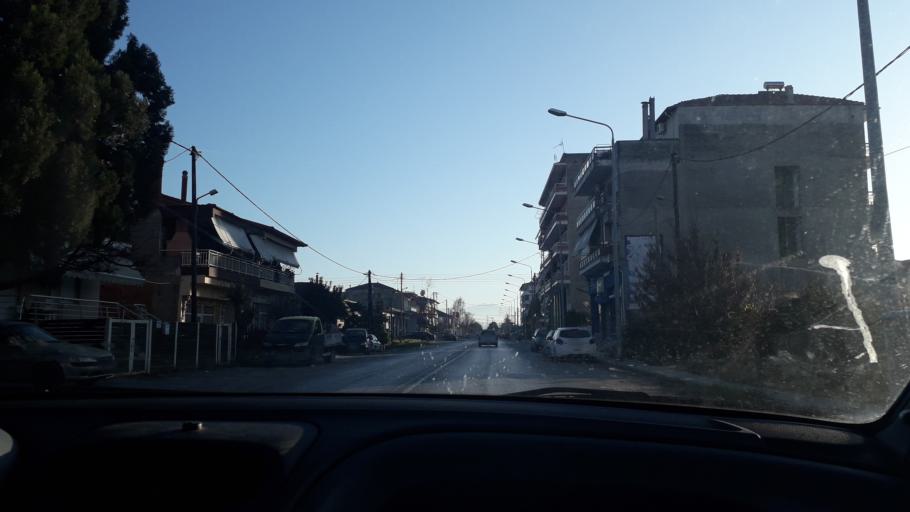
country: GR
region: Central Macedonia
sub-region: Nomos Imathias
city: Alexandreia
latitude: 40.6245
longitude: 22.4478
